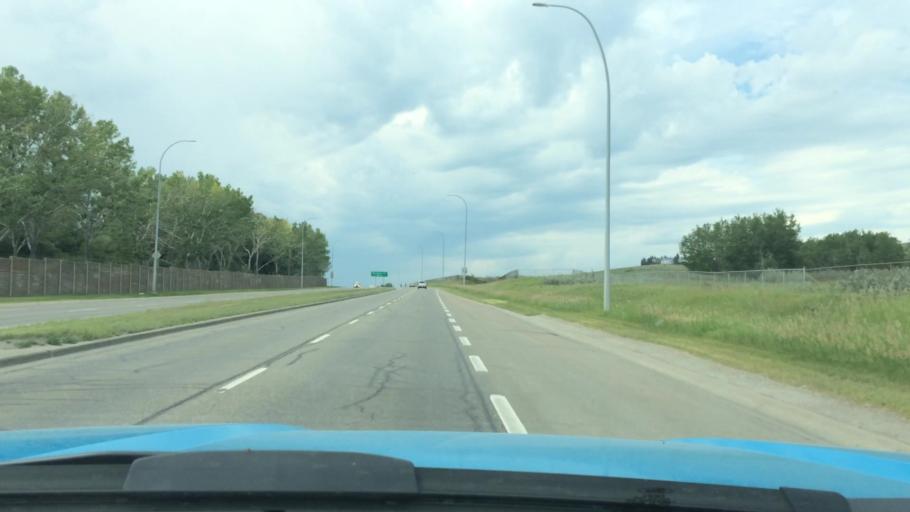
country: CA
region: Alberta
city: Calgary
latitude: 51.1038
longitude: -114.1283
